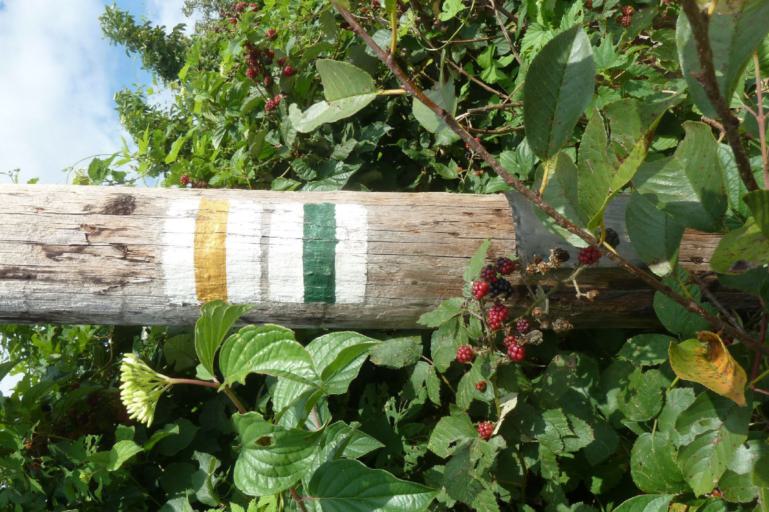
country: HU
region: Baranya
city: Harkany
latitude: 45.9064
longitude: 18.2479
